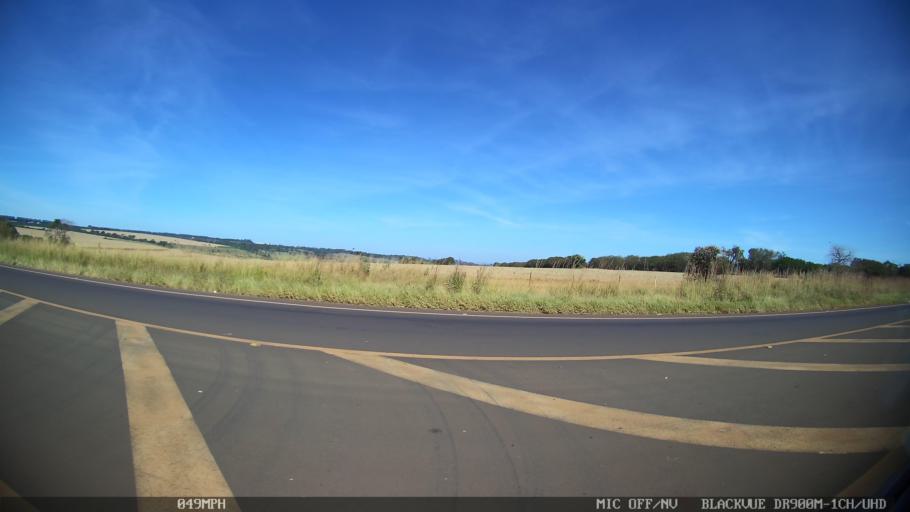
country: BR
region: Sao Paulo
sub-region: Franca
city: Franca
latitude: -20.5461
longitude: -47.4709
